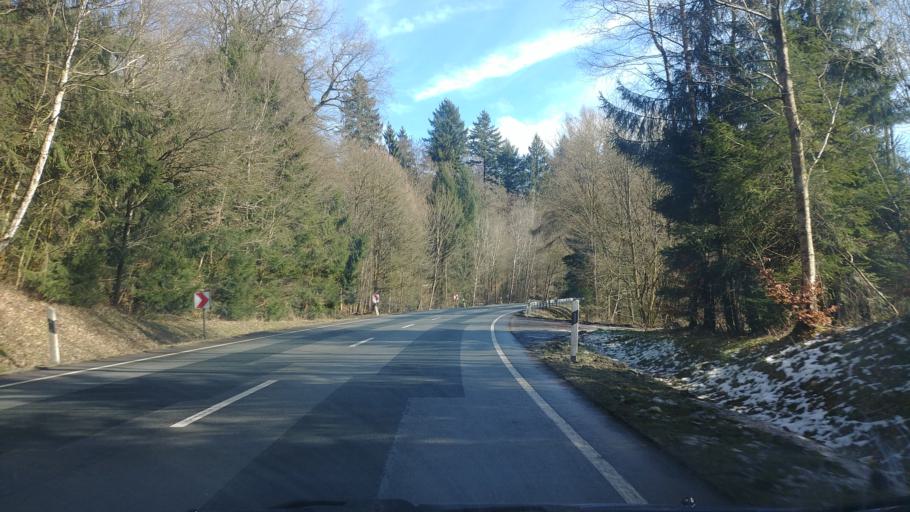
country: DE
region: Lower Saxony
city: Bodenfelde
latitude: 51.6950
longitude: 9.5331
